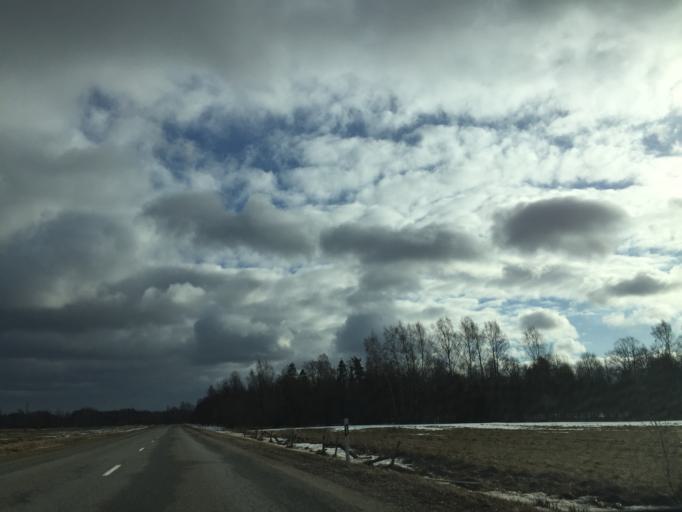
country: LV
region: Aloja
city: Staicele
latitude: 57.8683
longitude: 24.6858
